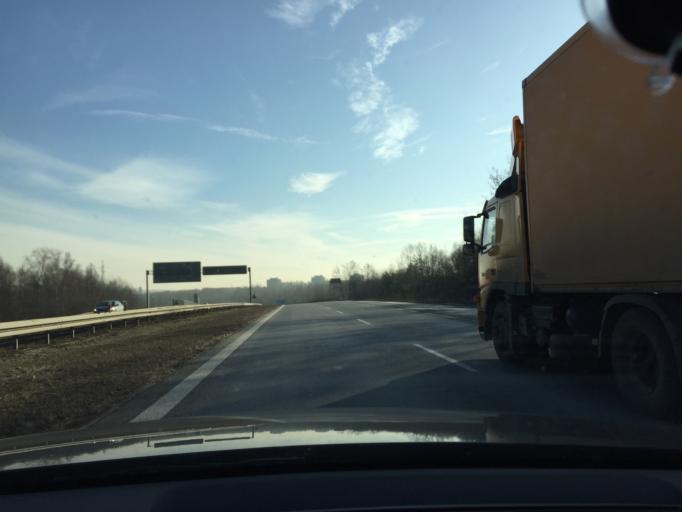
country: PL
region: Silesian Voivodeship
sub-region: Katowice
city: Murcki
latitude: 50.2356
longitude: 19.0613
